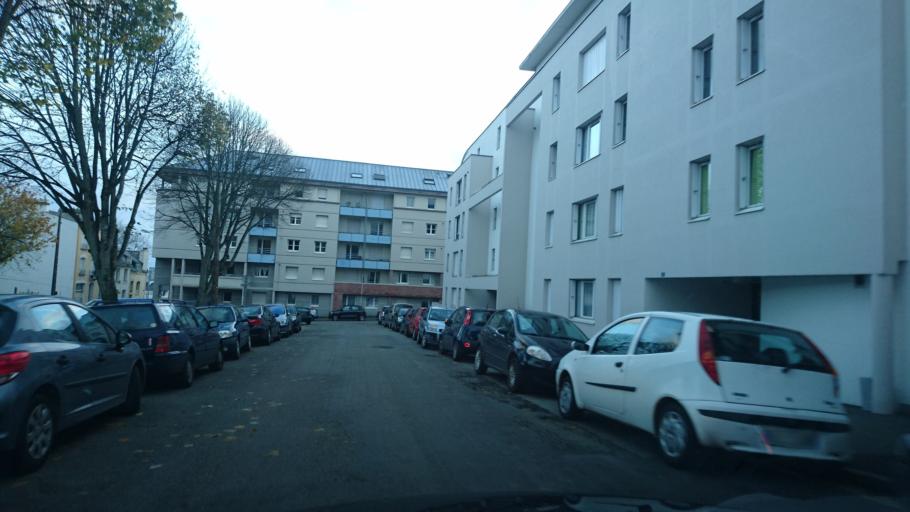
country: FR
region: Brittany
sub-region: Departement du Finistere
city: Brest
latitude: 48.3907
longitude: -4.4747
